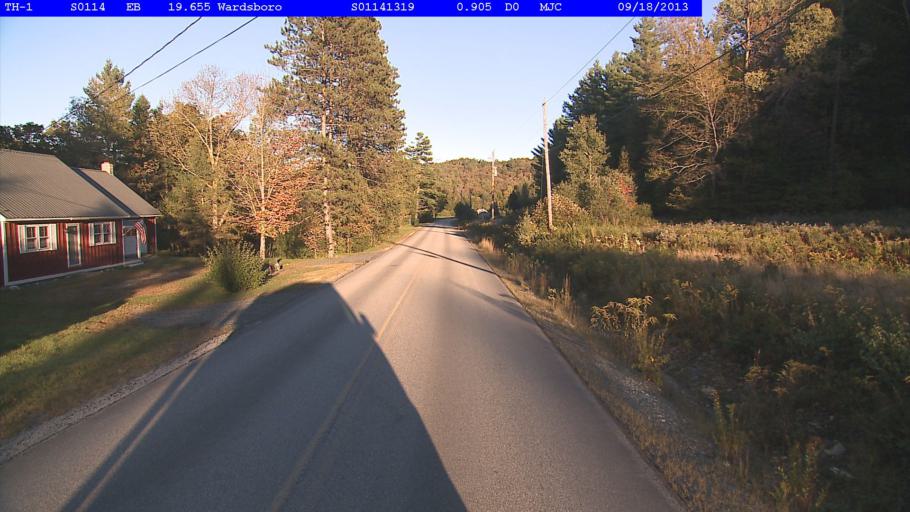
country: US
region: Vermont
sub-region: Windham County
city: Dover
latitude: 43.0293
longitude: -72.8585
